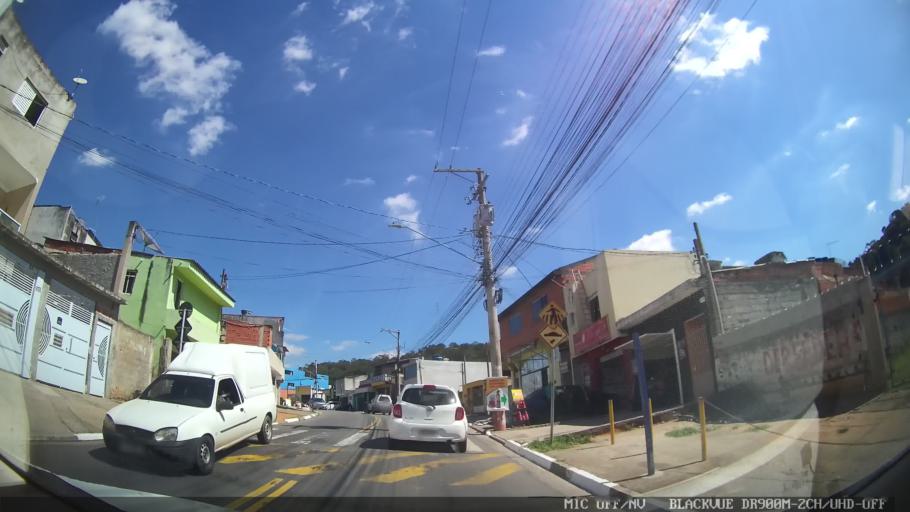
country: BR
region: Sao Paulo
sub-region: Cajamar
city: Cajamar
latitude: -23.4250
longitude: -46.8288
